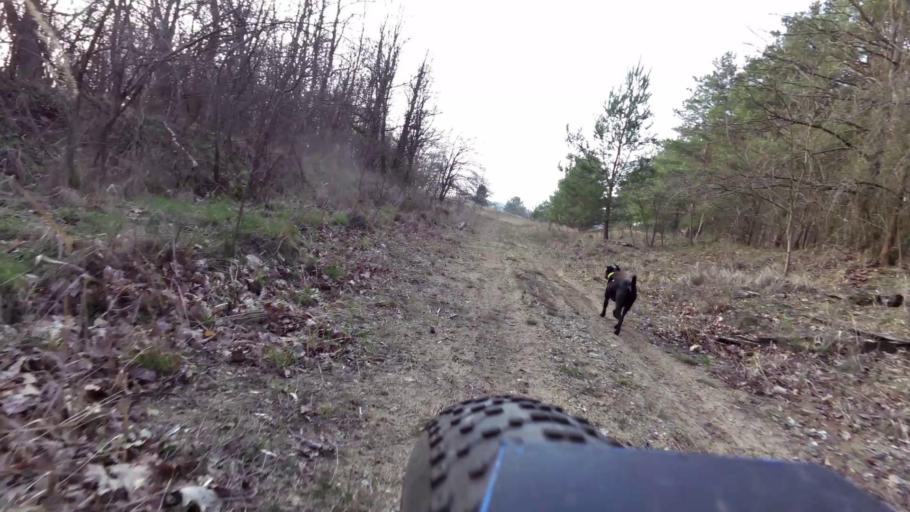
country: DE
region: Brandenburg
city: Vogelsang
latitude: 52.2582
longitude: 14.6943
